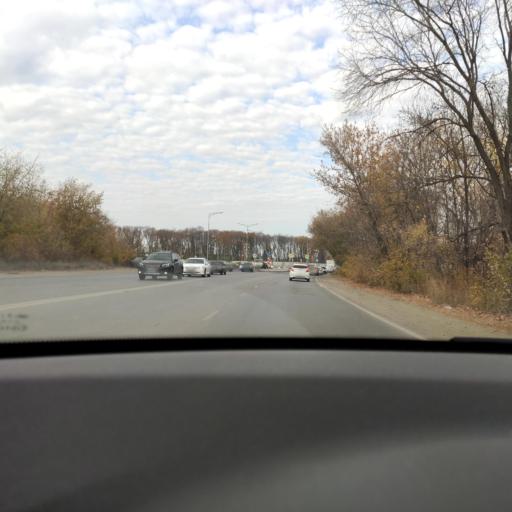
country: RU
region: Samara
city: Petra-Dubrava
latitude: 53.2737
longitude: 50.2673
